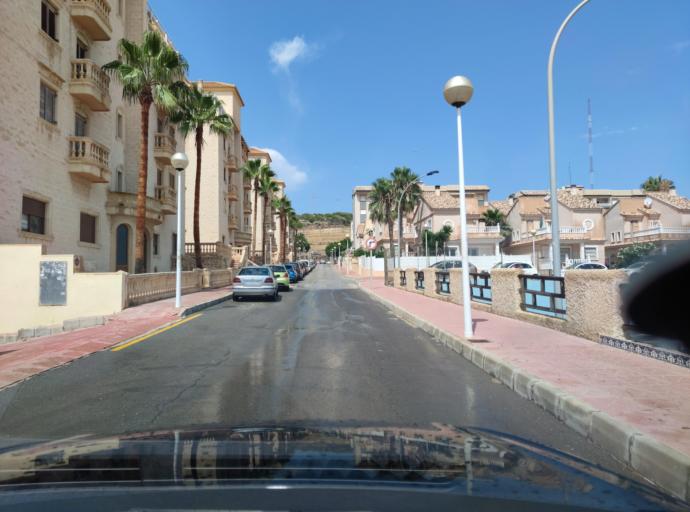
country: ES
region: Valencia
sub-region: Provincia de Alicante
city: Guardamar del Segura
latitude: 38.0652
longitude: -0.6528
